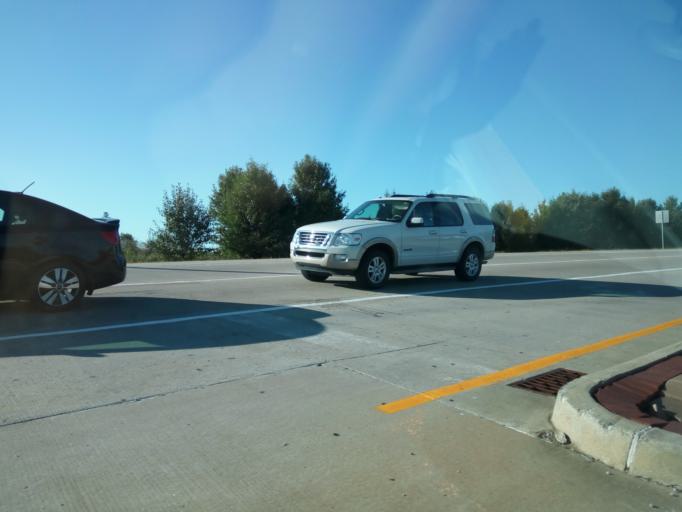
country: US
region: Kentucky
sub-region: Oldham County
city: Pewee Valley
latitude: 38.2741
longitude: -85.4908
